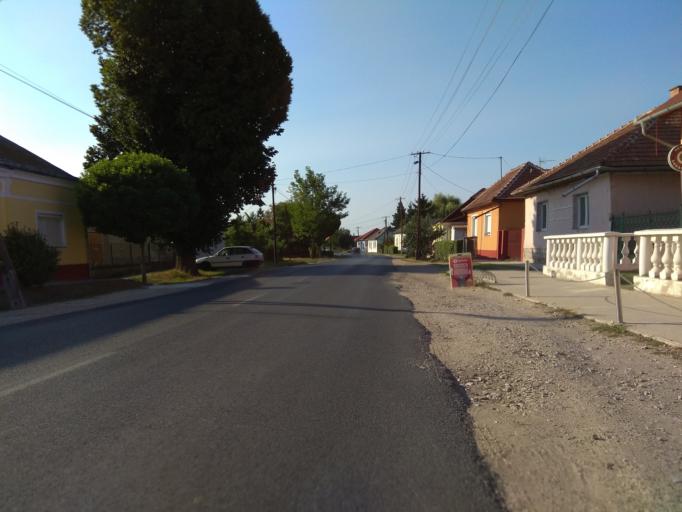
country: HU
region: Borsod-Abauj-Zemplen
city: Onod
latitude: 48.0039
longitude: 20.9171
